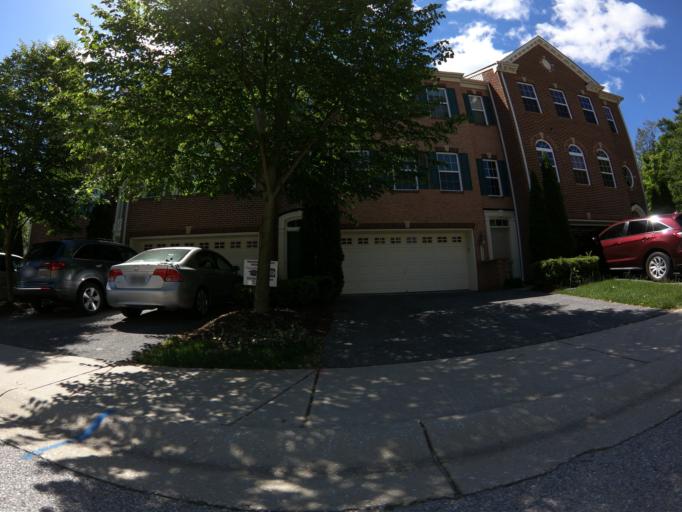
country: US
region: Maryland
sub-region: Howard County
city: Columbia
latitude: 39.3102
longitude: -76.8902
